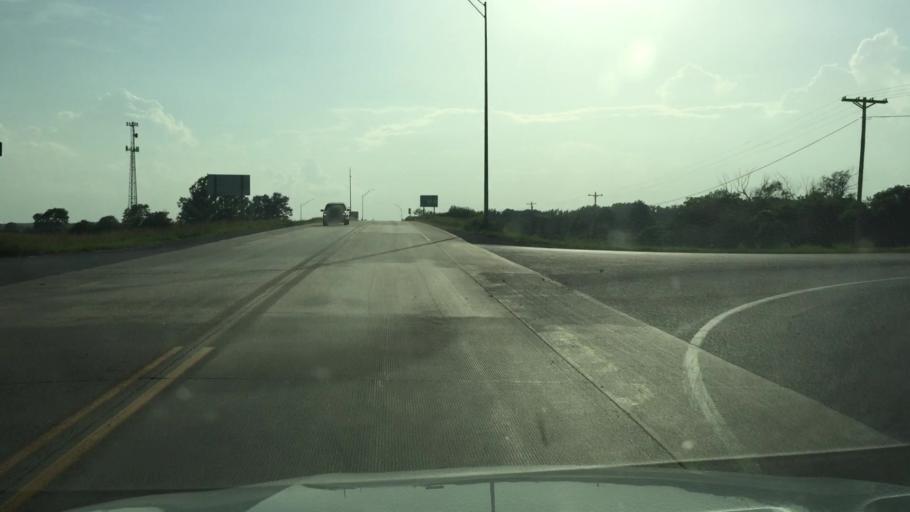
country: US
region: Iowa
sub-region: Linn County
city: Ely
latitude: 41.8479
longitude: -91.6652
